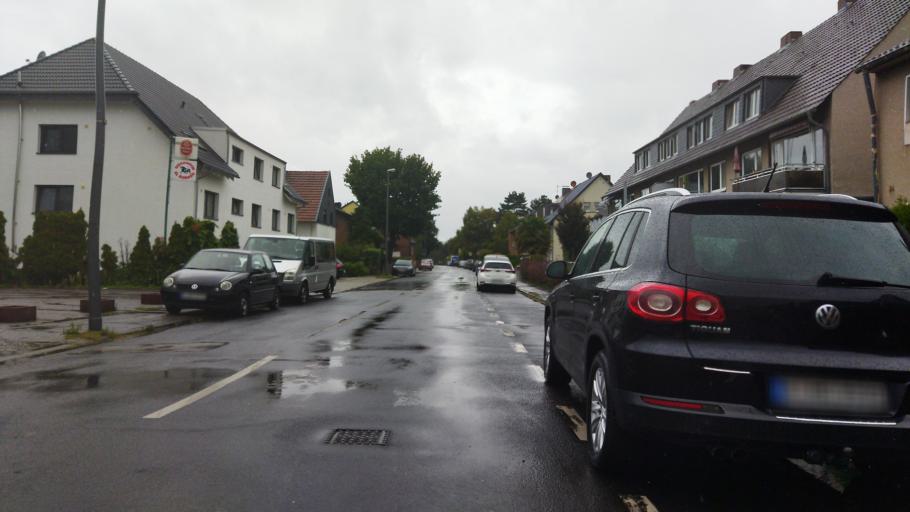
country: DE
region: North Rhine-Westphalia
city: Wesseling
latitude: 50.8493
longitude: 6.9726
